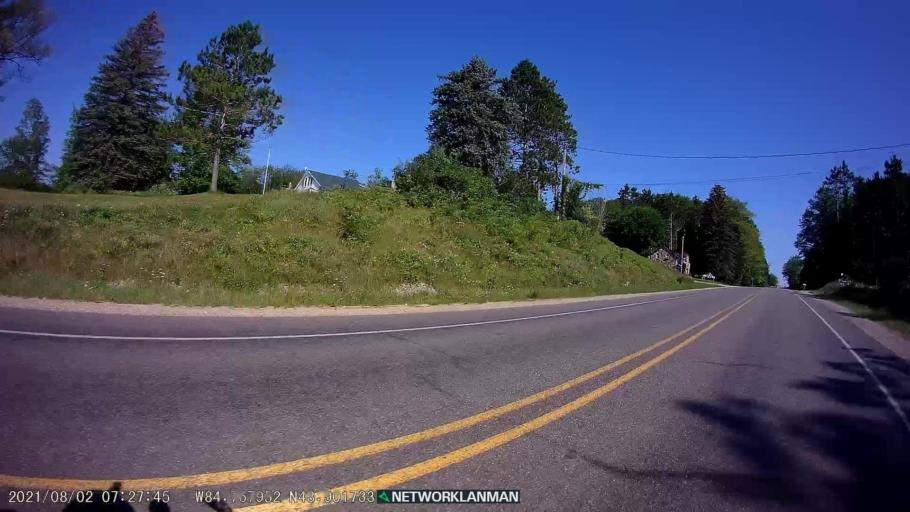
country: US
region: Michigan
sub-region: Clare County
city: Clare
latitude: 43.9013
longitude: -84.7680
